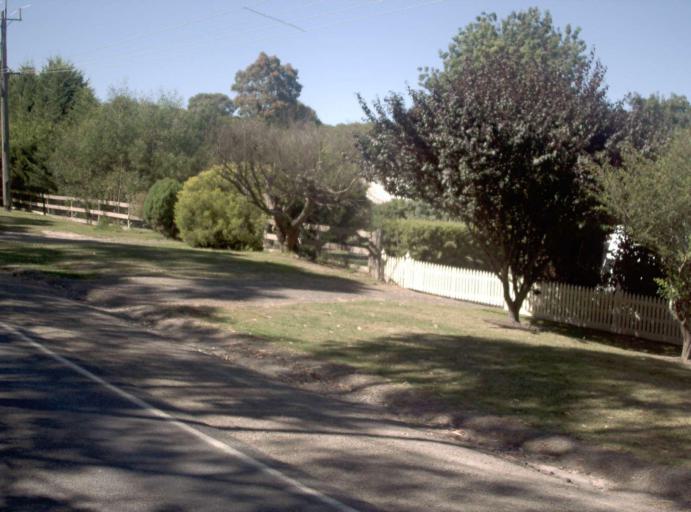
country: AU
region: Victoria
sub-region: Yarra Ranges
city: Healesville
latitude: -37.6741
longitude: 145.5399
